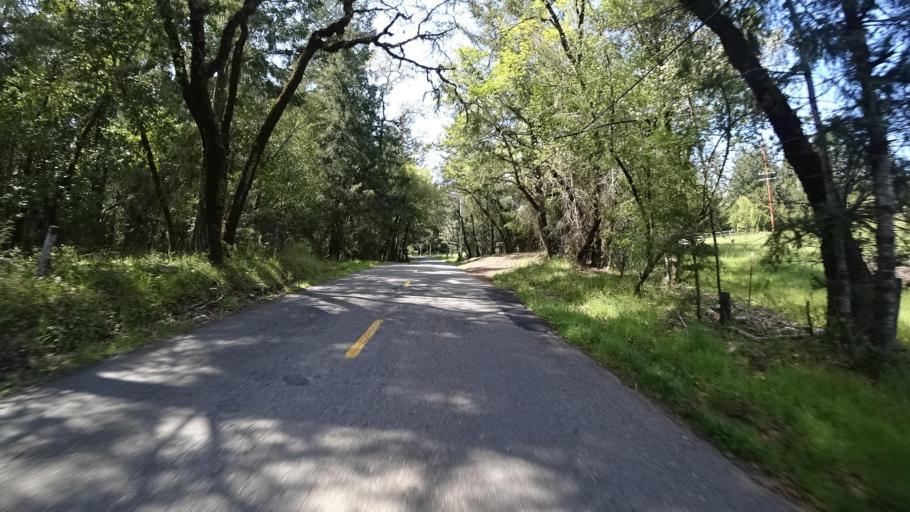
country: US
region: California
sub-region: Humboldt County
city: Redway
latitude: 40.3892
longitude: -123.7428
